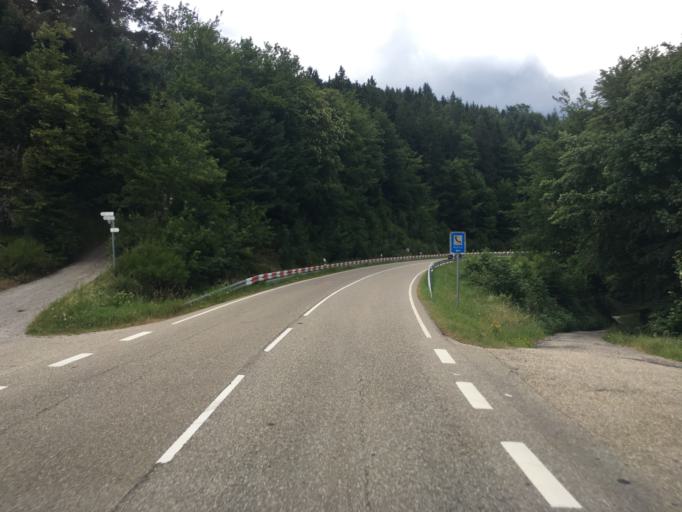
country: DE
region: Baden-Wuerttemberg
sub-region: Karlsruhe Region
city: Buhlertal
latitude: 48.6877
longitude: 8.2303
